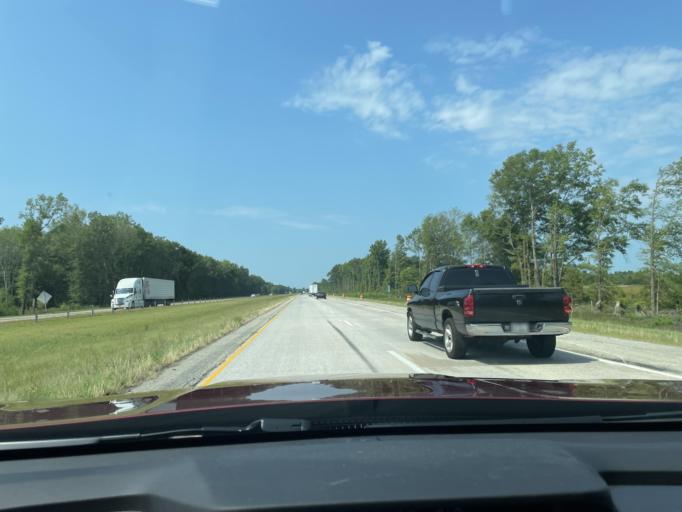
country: US
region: Arkansas
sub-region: White County
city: Searcy
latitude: 35.1613
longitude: -91.7806
